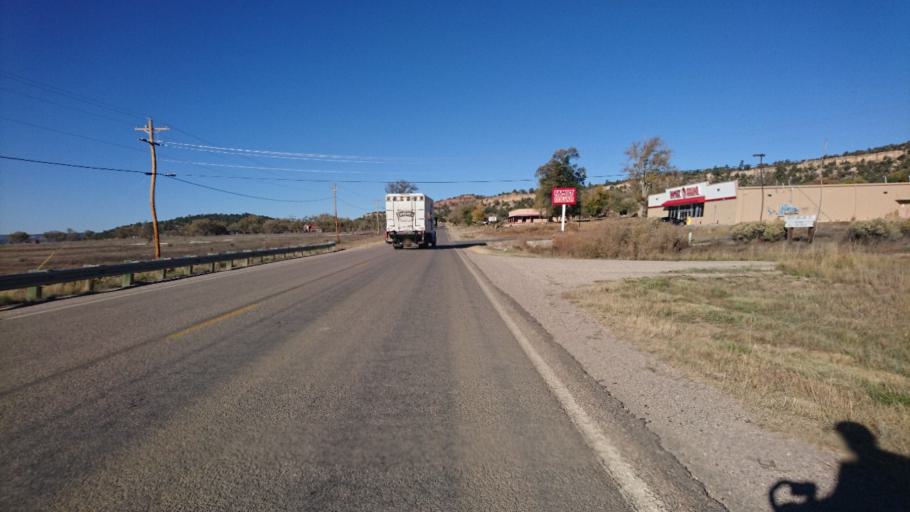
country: US
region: New Mexico
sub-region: McKinley County
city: Black Rock
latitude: 35.1333
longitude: -108.5080
